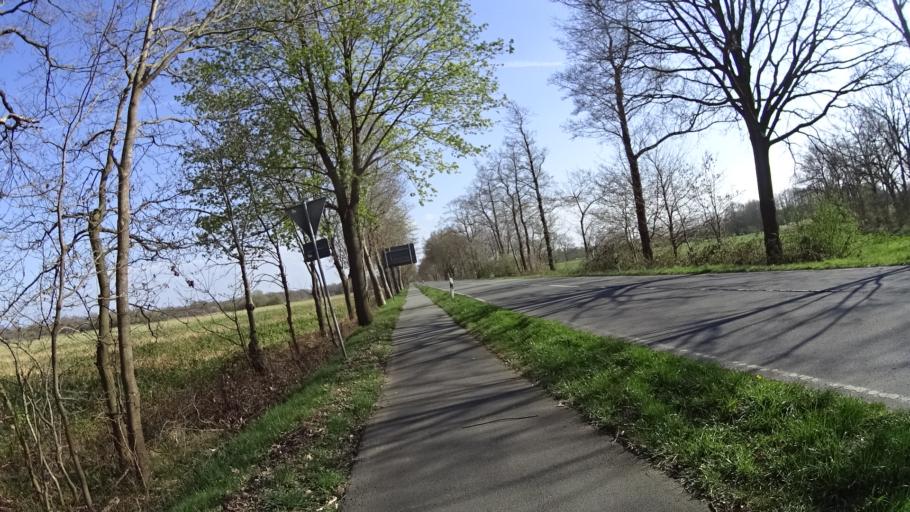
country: DE
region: Lower Saxony
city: Dorpen
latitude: 52.9772
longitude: 7.3089
